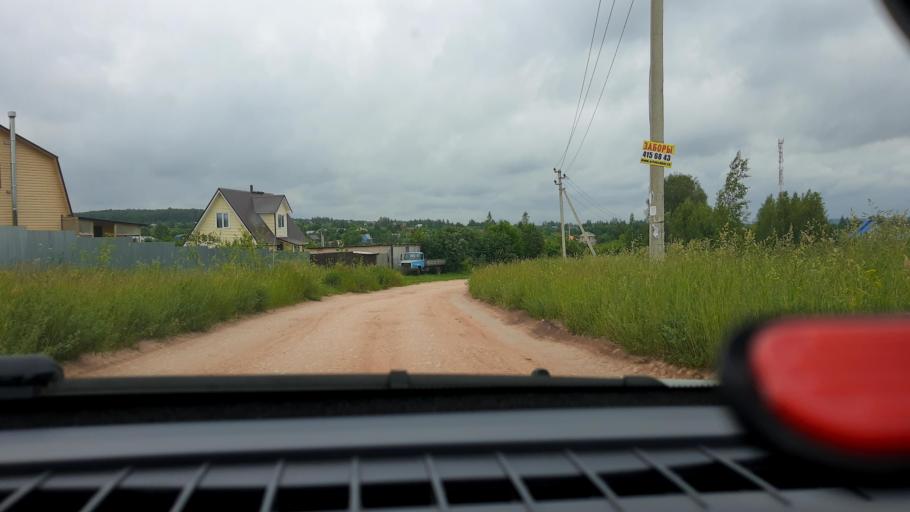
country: RU
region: Nizjnij Novgorod
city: Burevestnik
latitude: 56.1025
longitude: 43.9381
